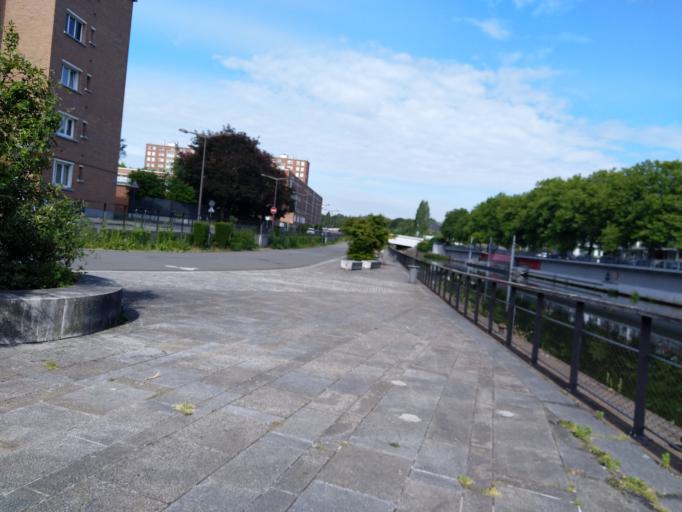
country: FR
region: Nord-Pas-de-Calais
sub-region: Departement du Nord
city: Maubeuge
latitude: 50.2765
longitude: 3.9726
